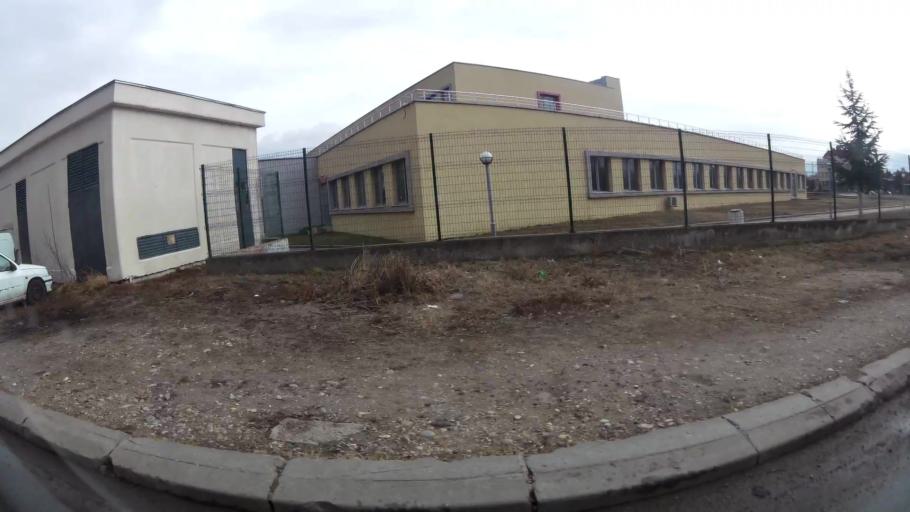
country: BG
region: Sofia-Capital
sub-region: Stolichna Obshtina
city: Sofia
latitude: 42.7459
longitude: 23.2730
